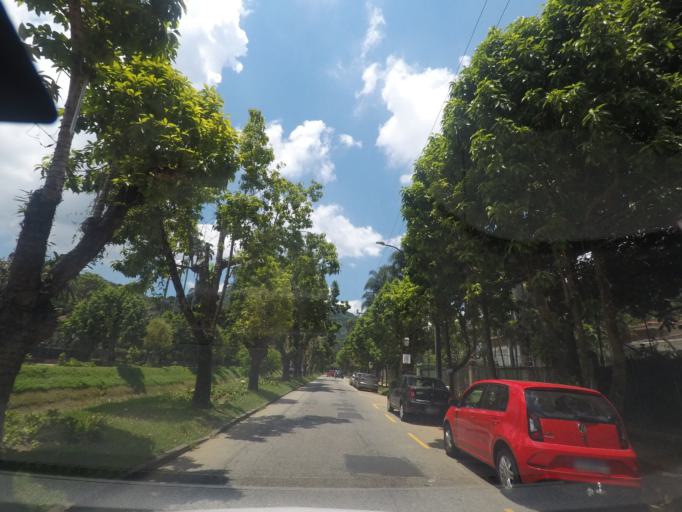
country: BR
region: Rio de Janeiro
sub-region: Petropolis
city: Petropolis
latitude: -22.5077
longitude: -43.1809
